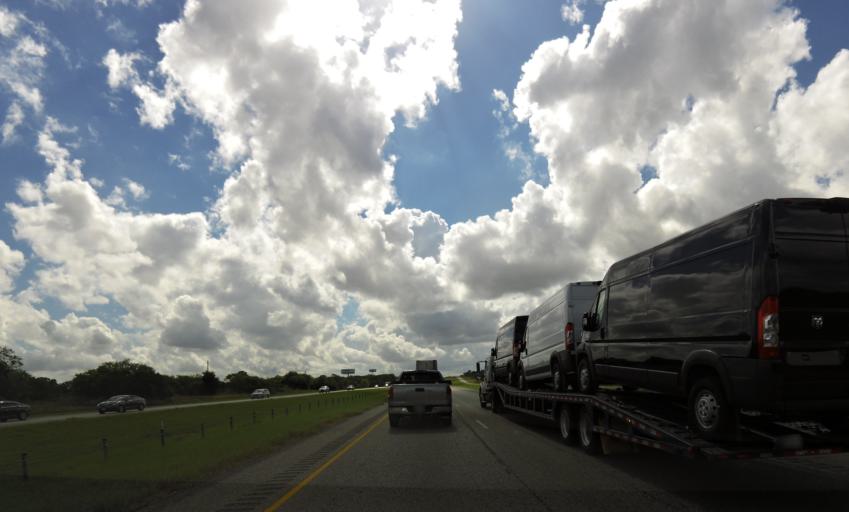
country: US
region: Texas
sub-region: Caldwell County
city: Luling
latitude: 29.6514
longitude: -97.5242
